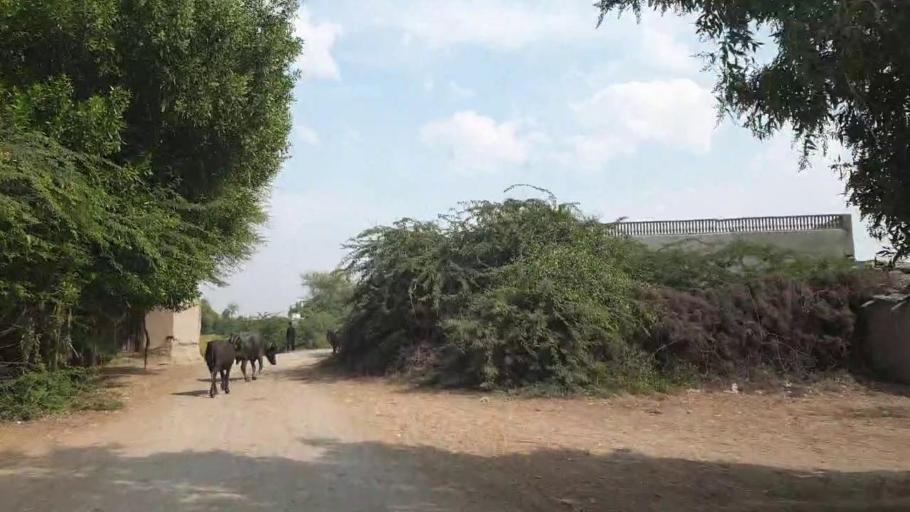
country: PK
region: Sindh
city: Rajo Khanani
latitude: 24.9370
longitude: 68.9952
